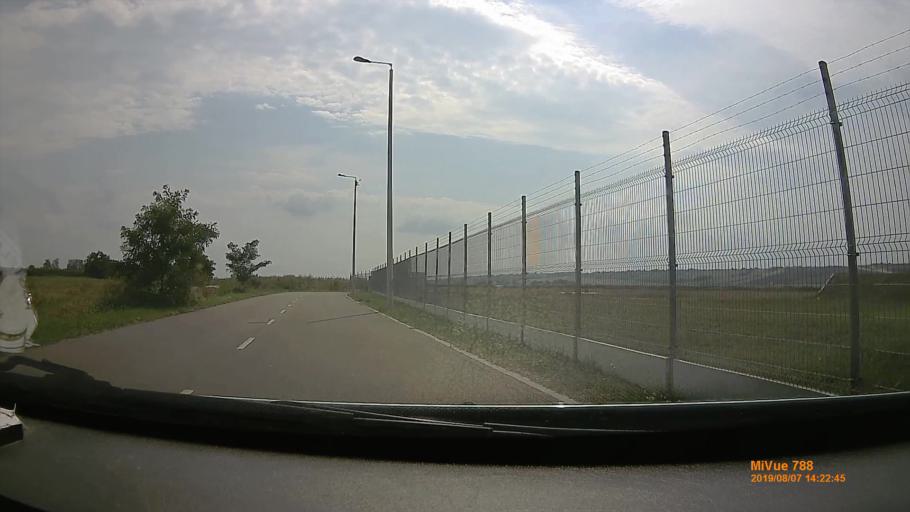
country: HU
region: Borsod-Abauj-Zemplen
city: Szikszo
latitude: 48.1728
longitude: 20.9237
